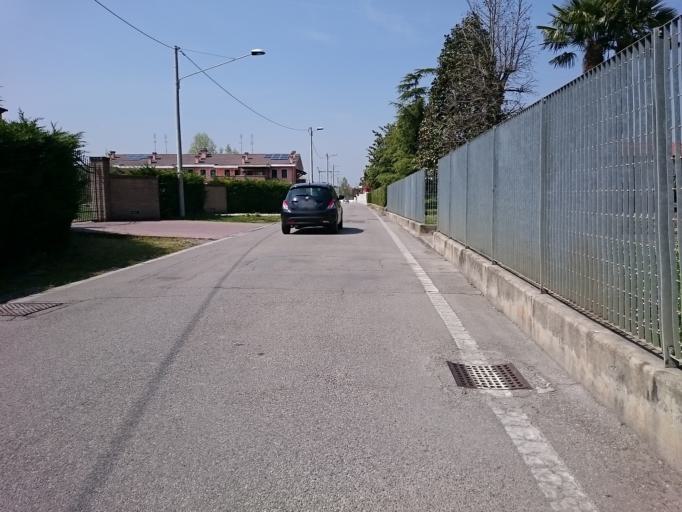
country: IT
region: Veneto
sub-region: Provincia di Padova
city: Albignasego
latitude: 45.3763
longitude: 11.8816
